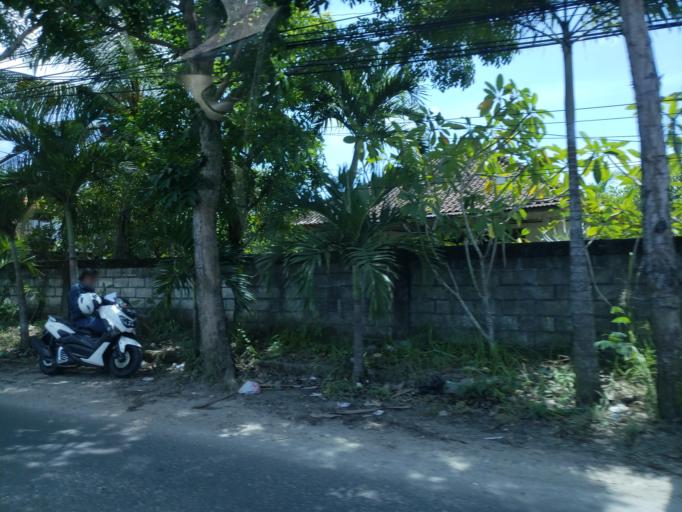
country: ID
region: Bali
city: Kangin
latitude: -8.8209
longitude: 115.1471
